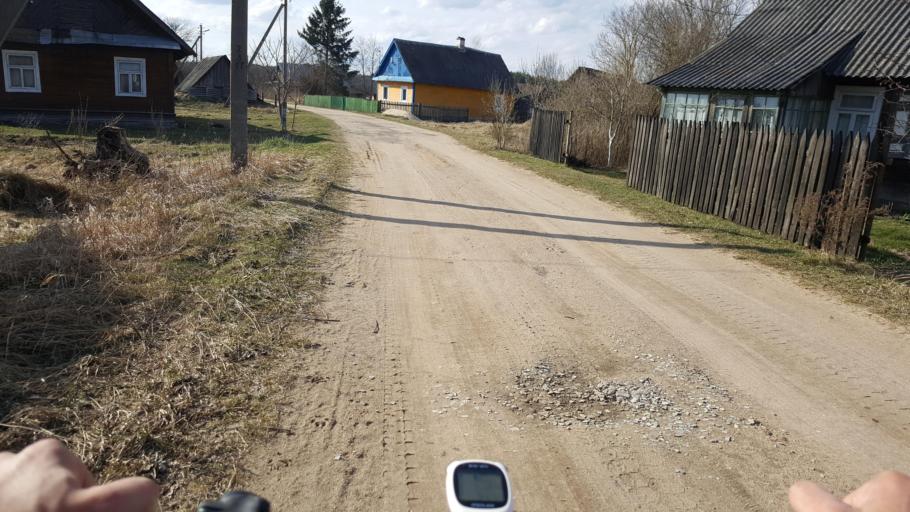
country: BY
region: Brest
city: Kamyanyets
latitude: 52.4175
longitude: 23.9223
